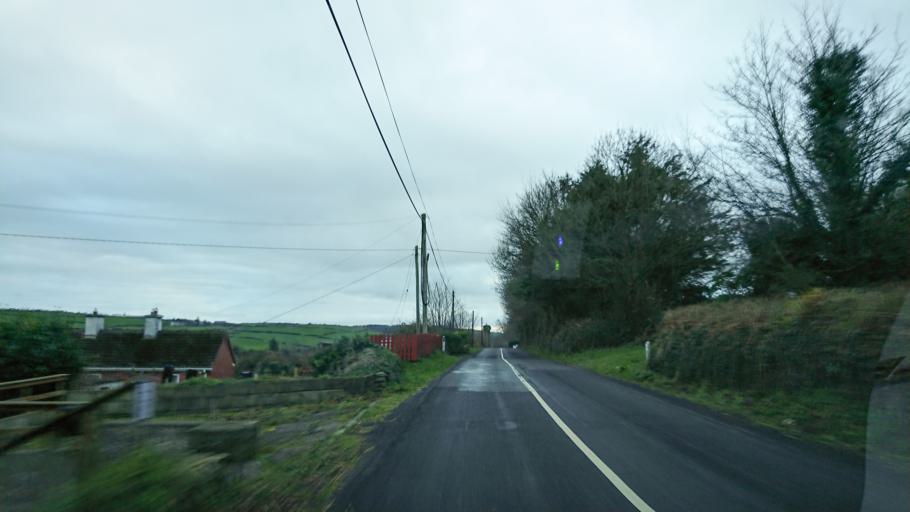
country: IE
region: Munster
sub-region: Waterford
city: Portlaw
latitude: 52.1674
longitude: -7.3909
